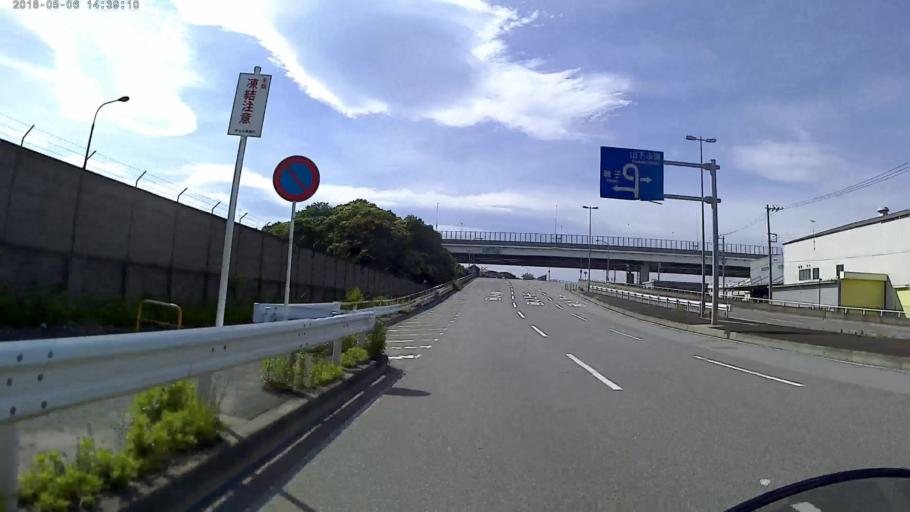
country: JP
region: Kanagawa
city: Yokohama
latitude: 35.4146
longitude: 139.6695
